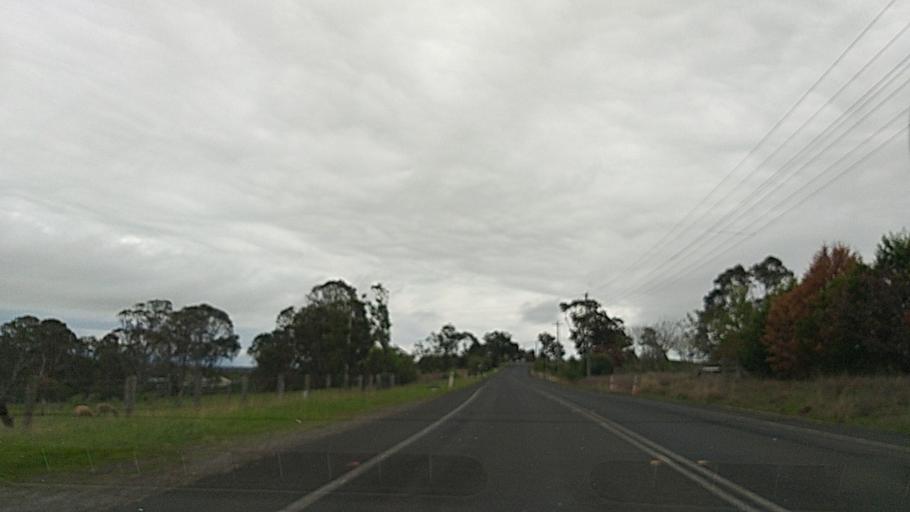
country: AU
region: New South Wales
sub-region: Wollondilly
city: Douglas Park
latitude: -34.1557
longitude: 150.7222
